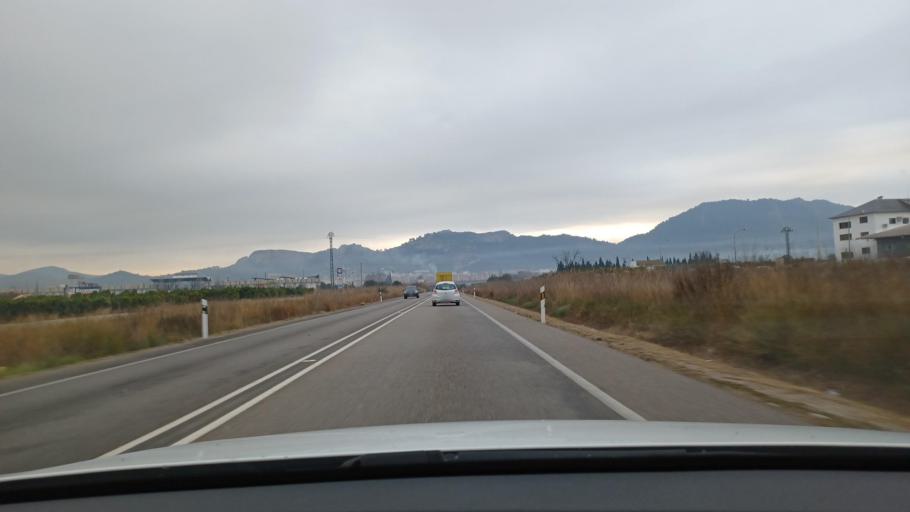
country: ES
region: Valencia
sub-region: Provincia de Valencia
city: Llosa de Ranes
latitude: 39.0075
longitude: -0.5318
